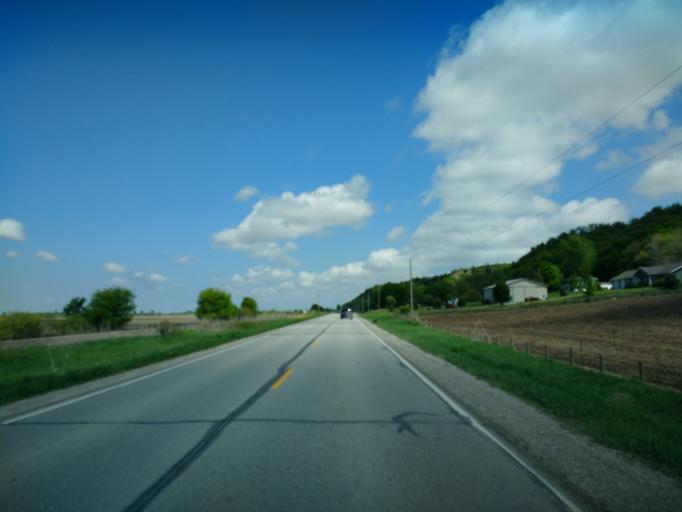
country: US
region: Iowa
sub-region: Harrison County
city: Missouri Valley
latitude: 41.4747
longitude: -95.8817
